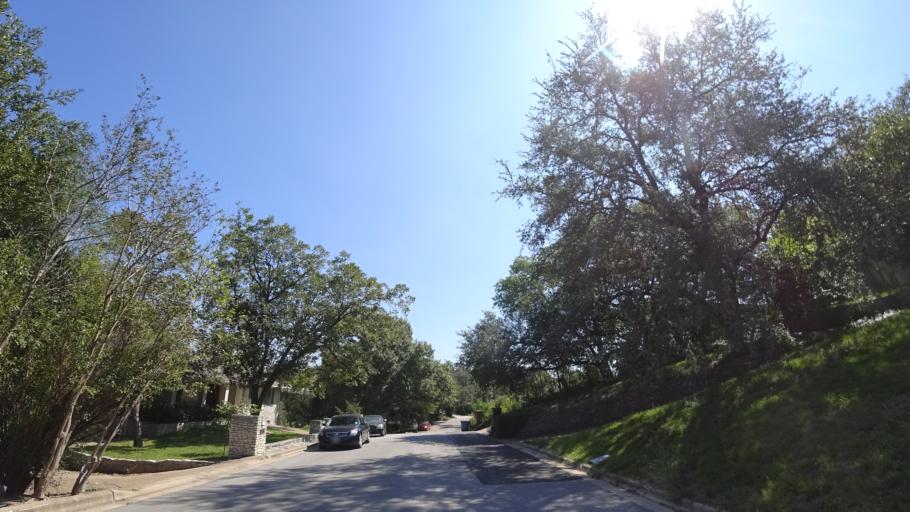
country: US
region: Texas
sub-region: Travis County
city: Rollingwood
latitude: 30.2758
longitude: -97.7839
